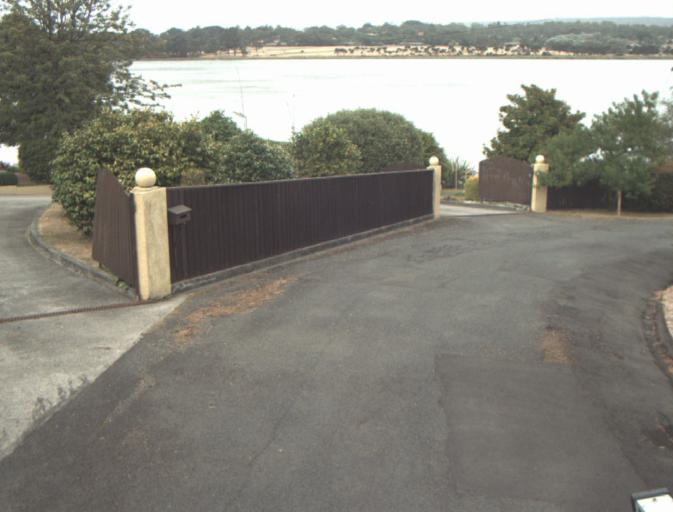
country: AU
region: Tasmania
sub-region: Launceston
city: Mayfield
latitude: -41.3299
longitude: 147.0673
